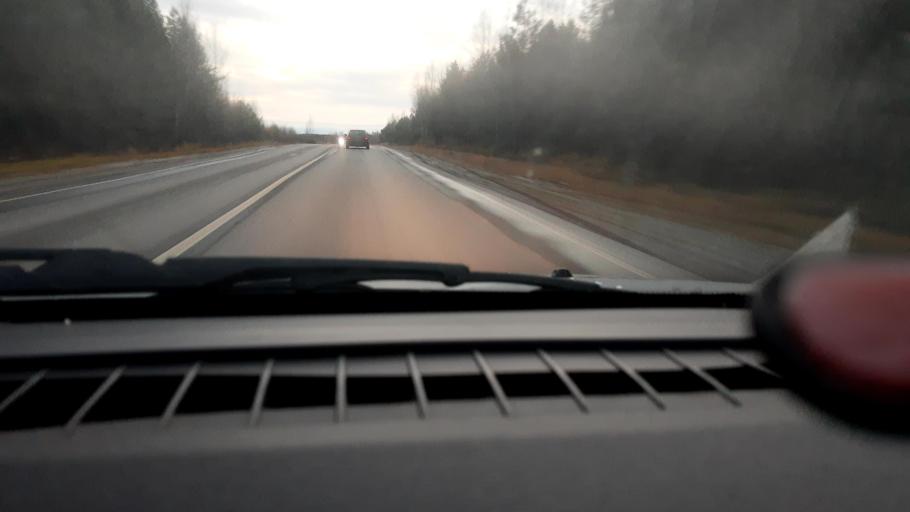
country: RU
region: Nizjnij Novgorod
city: Vladimirskoye
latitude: 56.9671
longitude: 45.1098
